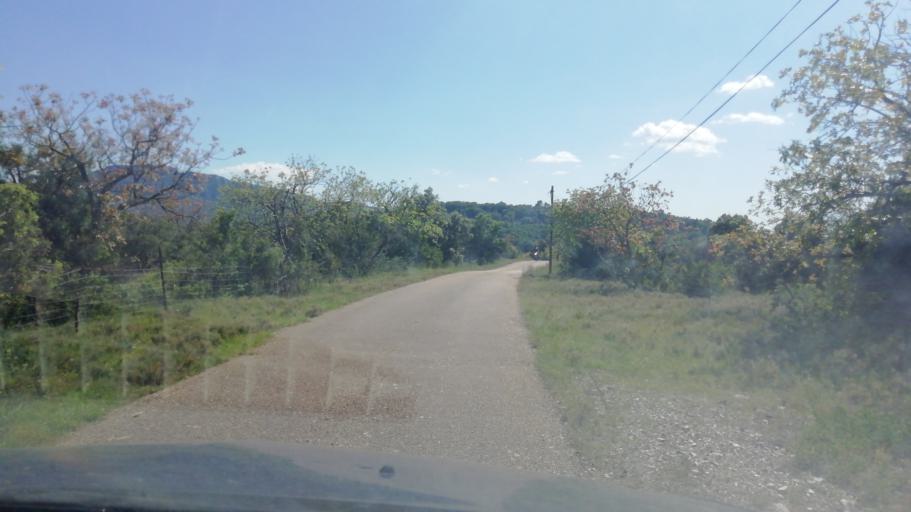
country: FR
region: Languedoc-Roussillon
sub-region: Departement de l'Herault
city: Saint-Mathieu-de-Treviers
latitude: 43.8265
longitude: 3.8134
